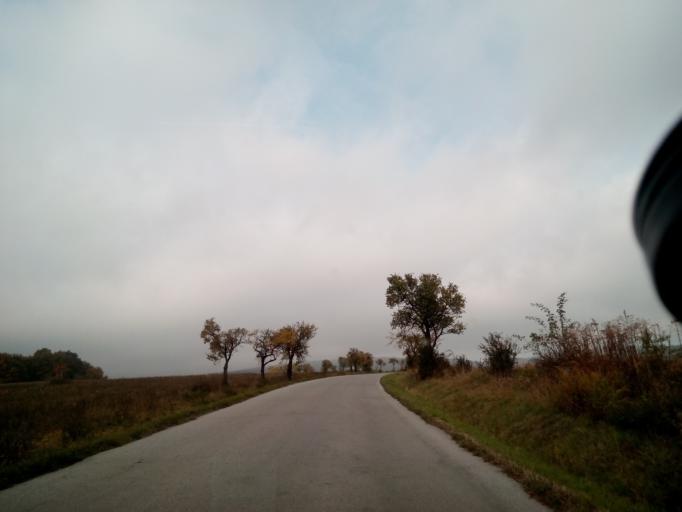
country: SK
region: Kosicky
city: Kosice
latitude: 48.7336
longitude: 21.1300
